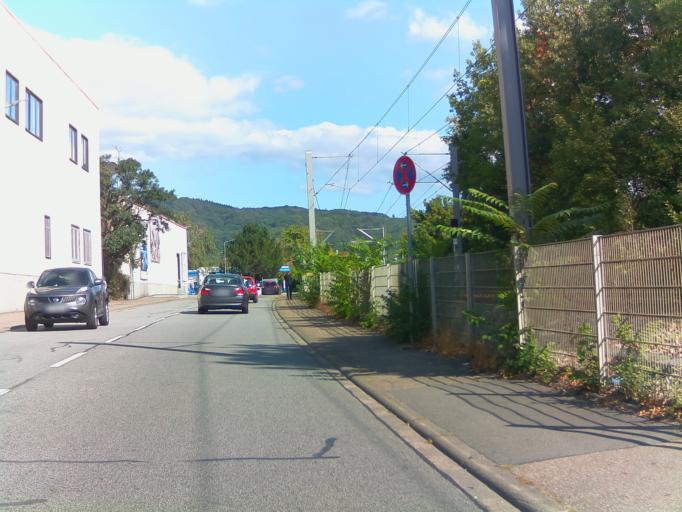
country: DE
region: Baden-Wuerttemberg
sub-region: Karlsruhe Region
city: Weinheim
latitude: 49.5473
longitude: 8.6523
